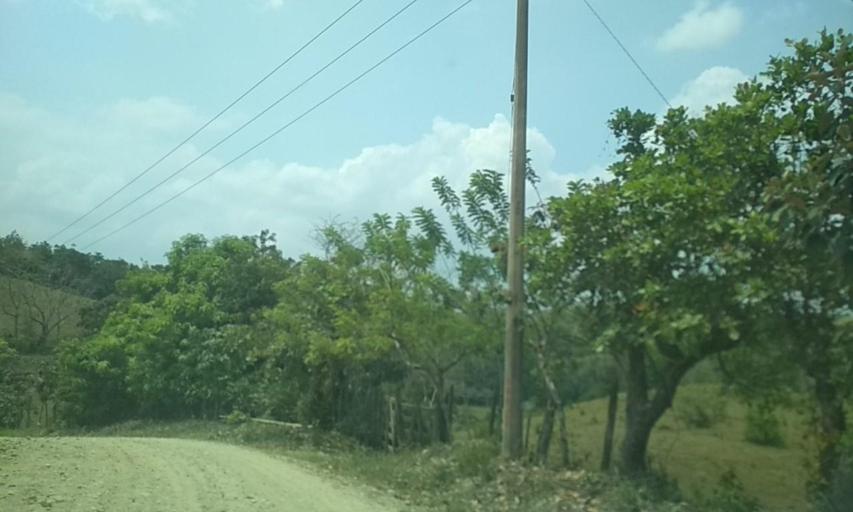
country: MX
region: Tabasco
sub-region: Huimanguillo
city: Francisco Rueda
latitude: 17.6371
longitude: -93.8228
